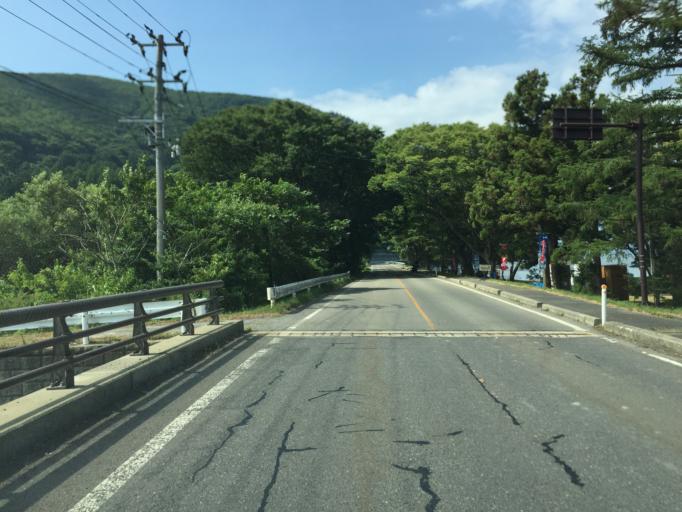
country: JP
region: Fukushima
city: Inawashiro
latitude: 37.4856
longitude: 140.1547
